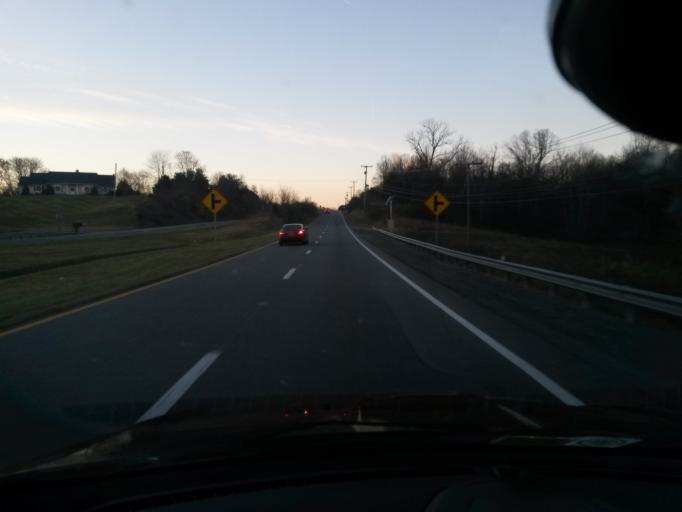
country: US
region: Virginia
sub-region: Botetourt County
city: Fincastle
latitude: 37.4760
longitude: -79.8805
